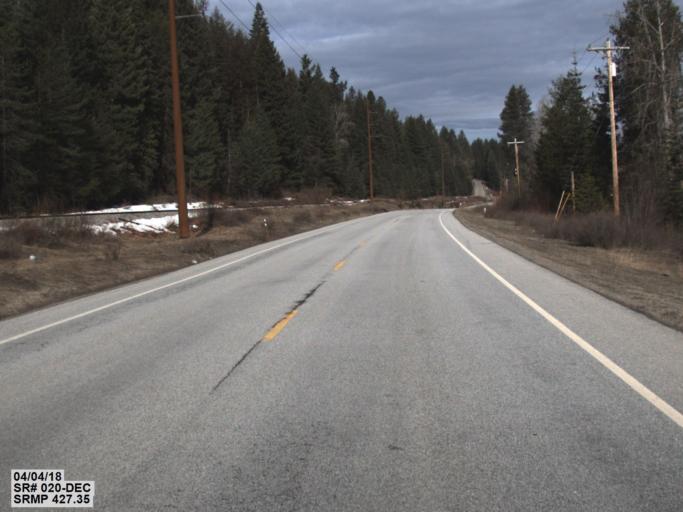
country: US
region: Washington
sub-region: Pend Oreille County
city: Newport
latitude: 48.2337
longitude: -117.2186
